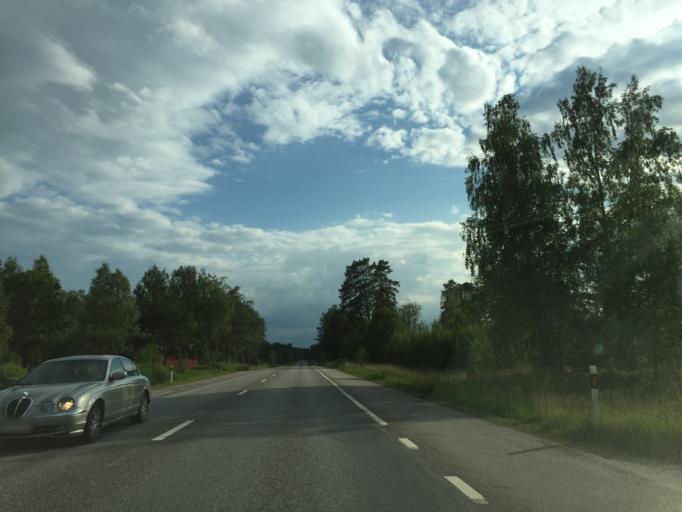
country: SE
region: OErebro
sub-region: Lindesbergs Kommun
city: Fellingsbro
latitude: 59.3617
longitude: 15.6911
